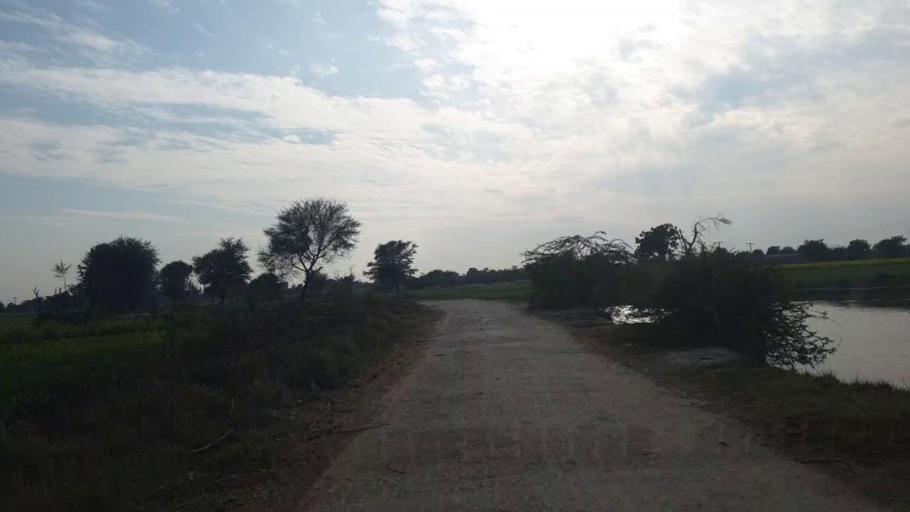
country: PK
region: Sindh
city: Shahpur Chakar
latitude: 26.0549
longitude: 68.5681
